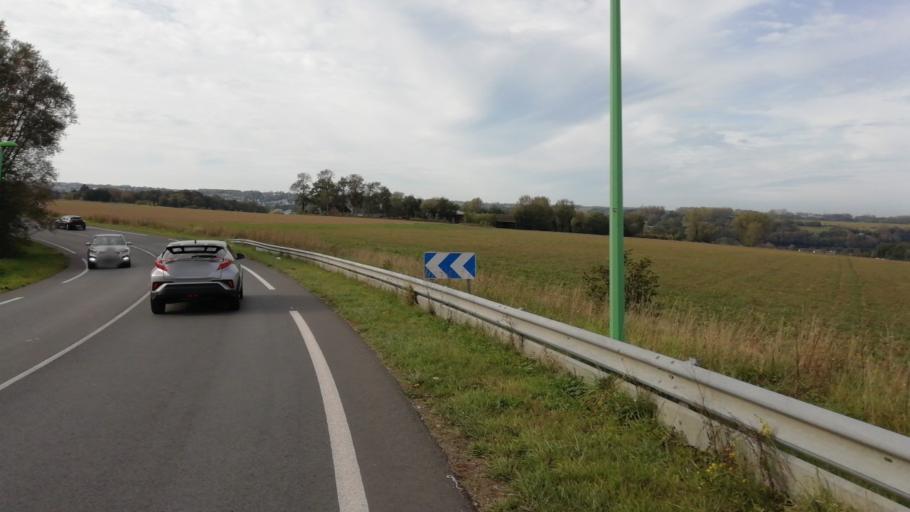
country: FR
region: Haute-Normandie
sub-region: Departement de la Seine-Maritime
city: Epouville
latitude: 49.5423
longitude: 0.2157
